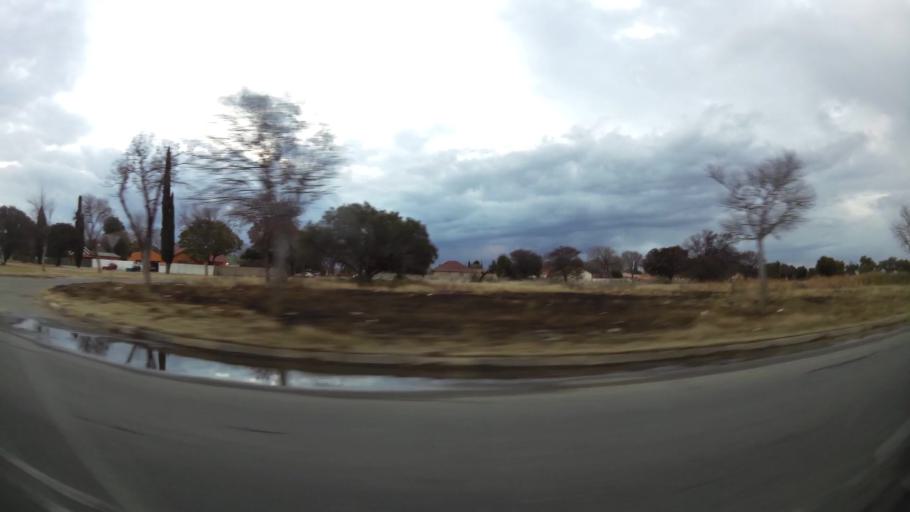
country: ZA
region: Orange Free State
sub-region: Lejweleputswa District Municipality
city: Welkom
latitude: -27.9620
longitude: 26.7516
